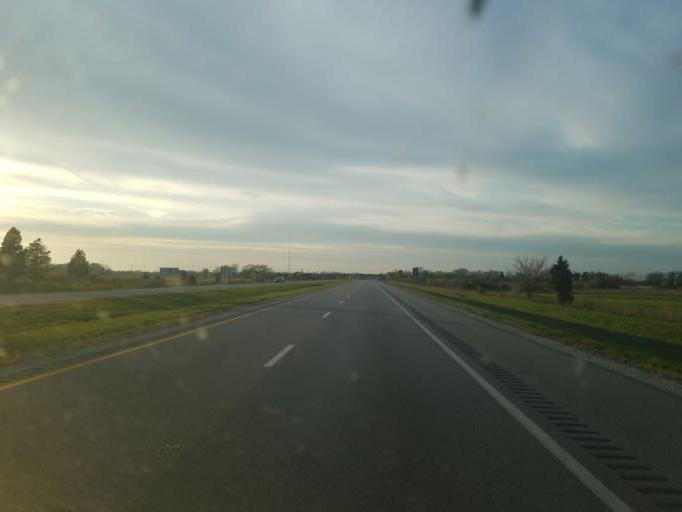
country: US
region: Ohio
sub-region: Wood County
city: Walbridge
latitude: 41.5737
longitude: -83.4687
